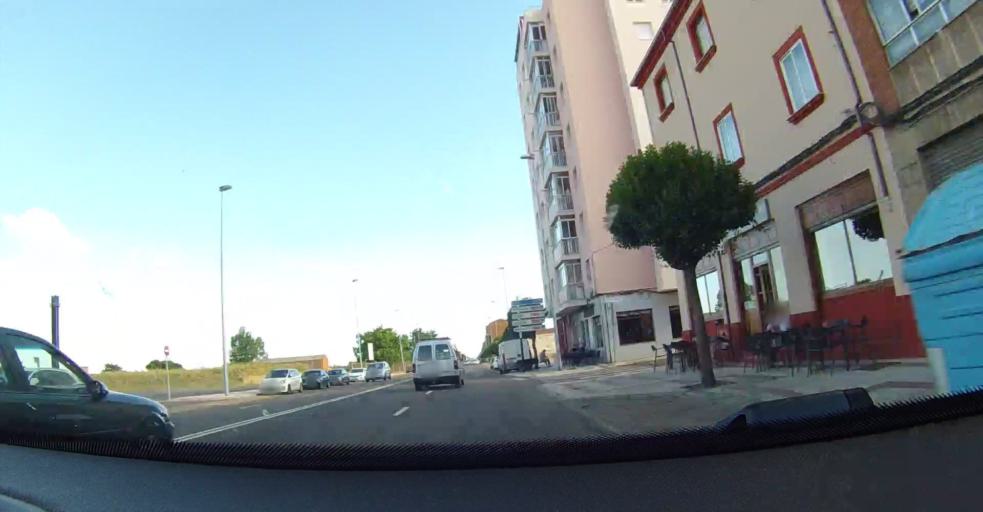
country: ES
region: Castille and Leon
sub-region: Provincia de Leon
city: Leon
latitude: 42.5927
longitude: -5.5851
